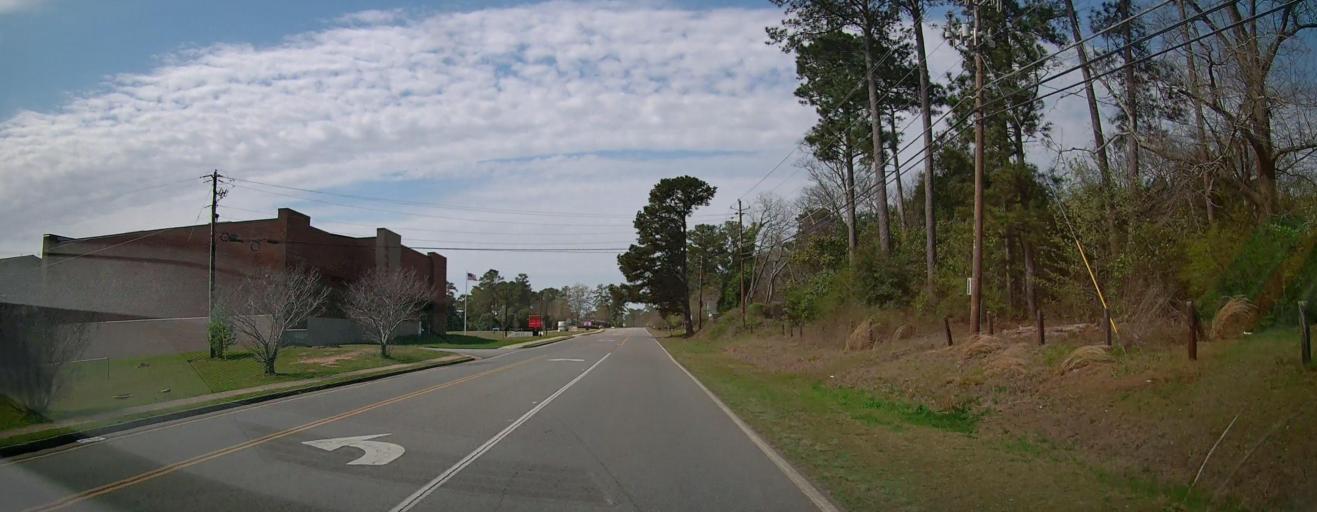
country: US
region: Georgia
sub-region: Bibb County
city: Macon
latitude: 32.8665
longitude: -83.6187
